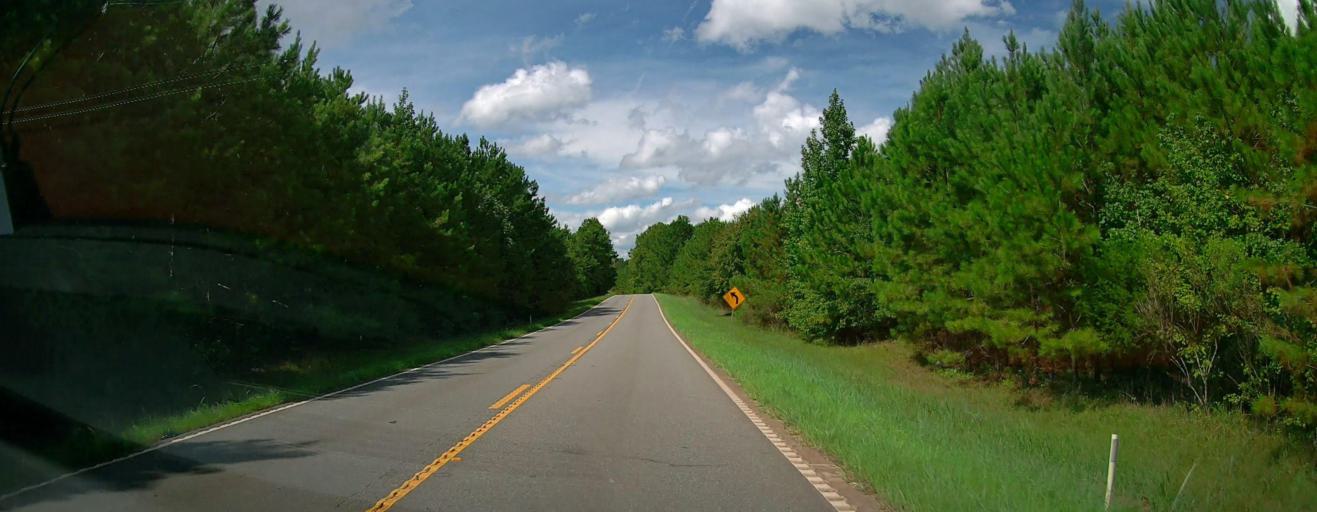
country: US
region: Georgia
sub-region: Talbot County
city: Talbotton
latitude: 32.6523
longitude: -84.5067
